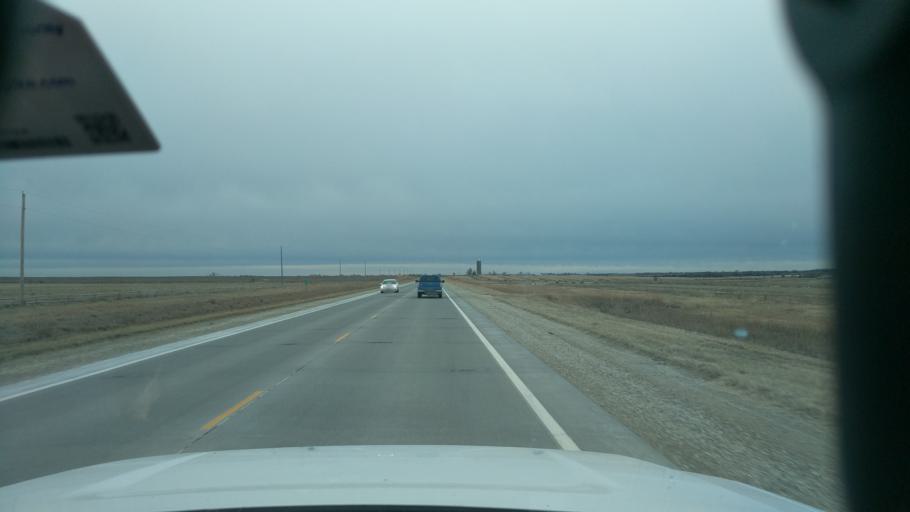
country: US
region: Kansas
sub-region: Dickinson County
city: Herington
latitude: 38.5839
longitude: -96.9482
